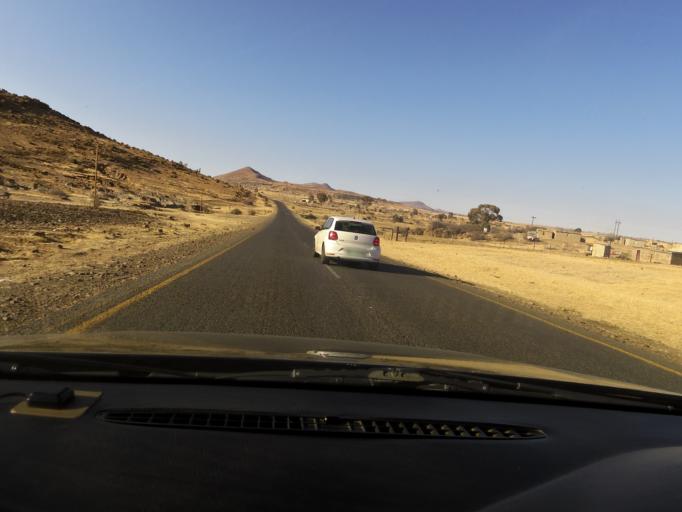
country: LS
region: Mafeteng
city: Mafeteng
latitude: -29.8656
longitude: 27.2365
